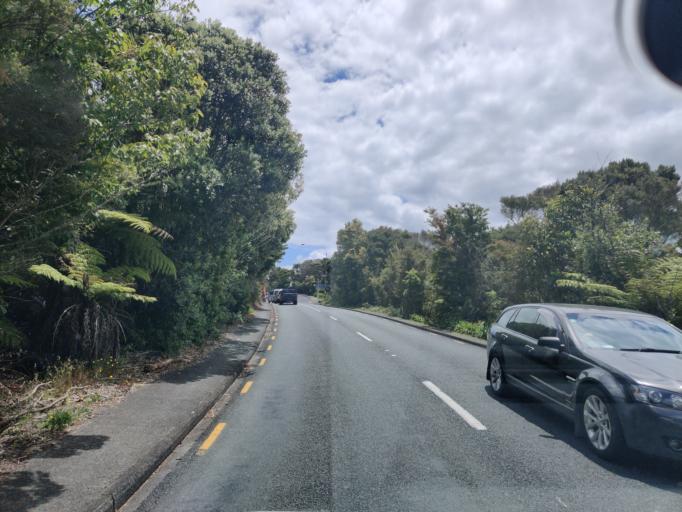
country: NZ
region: Northland
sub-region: Far North District
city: Paihia
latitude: -35.3134
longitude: 174.1137
